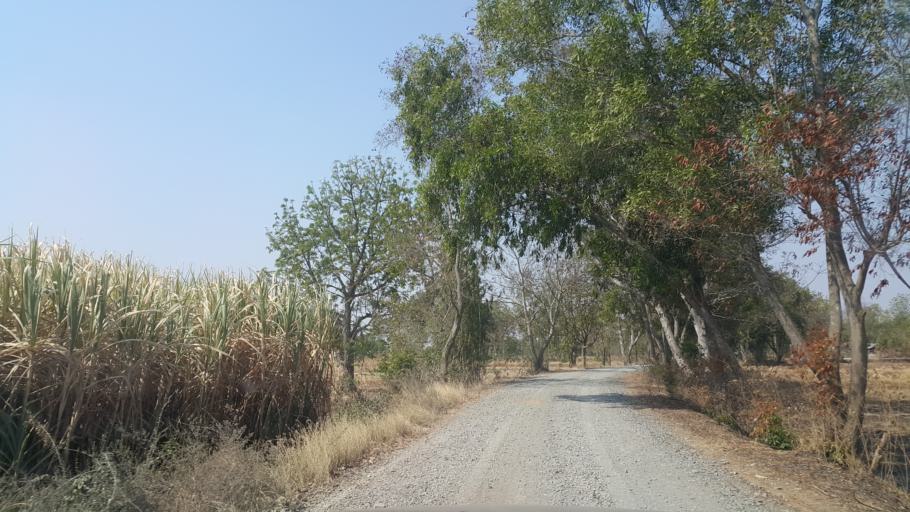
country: TH
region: Buriram
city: Krasang
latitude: 15.0909
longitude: 103.3775
